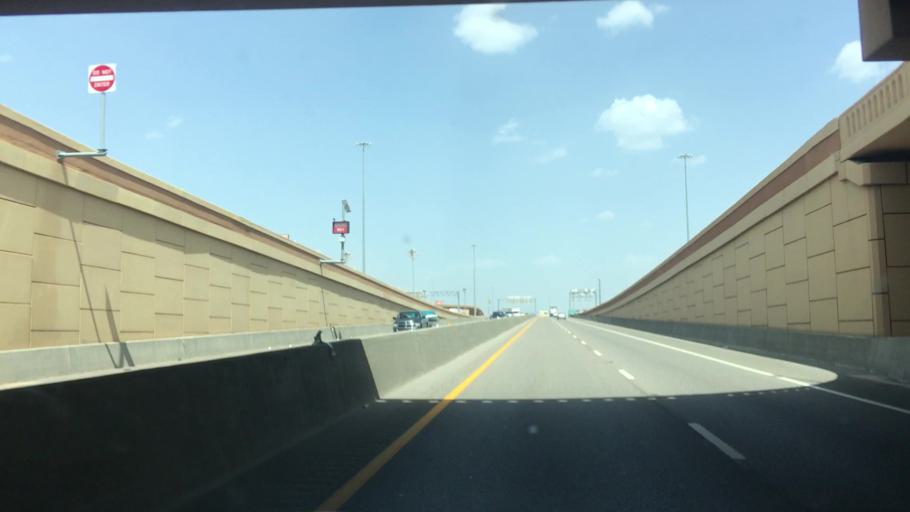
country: US
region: Texas
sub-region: Tarrant County
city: Watauga
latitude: 32.8402
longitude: -97.2512
